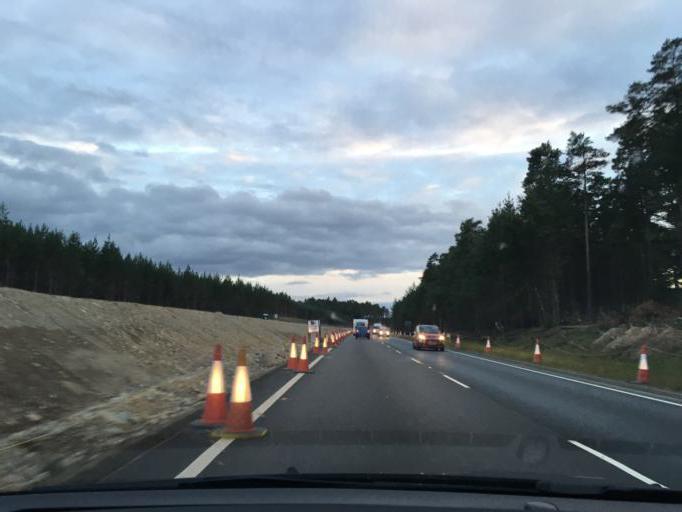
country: GB
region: Scotland
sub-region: Highland
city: Aviemore
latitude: 57.1466
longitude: -3.9079
